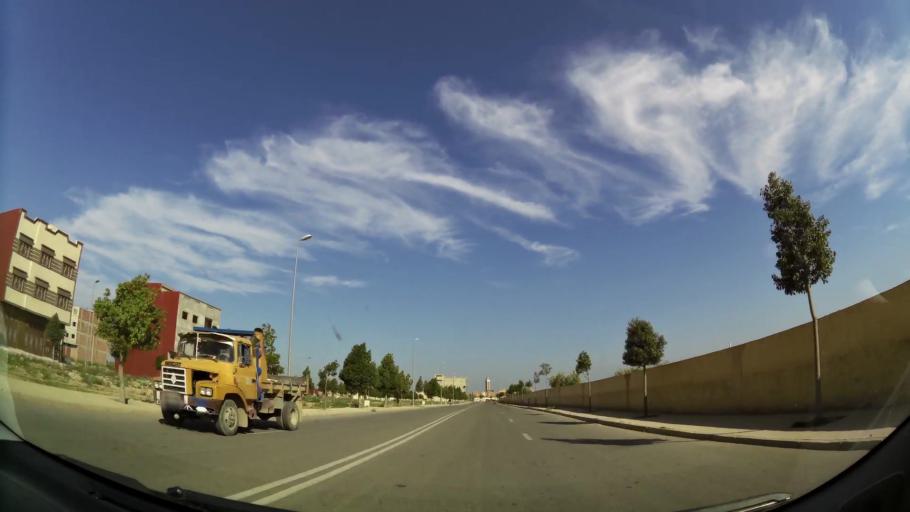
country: MA
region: Oriental
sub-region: Oujda-Angad
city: Oujda
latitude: 34.7153
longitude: -1.8888
